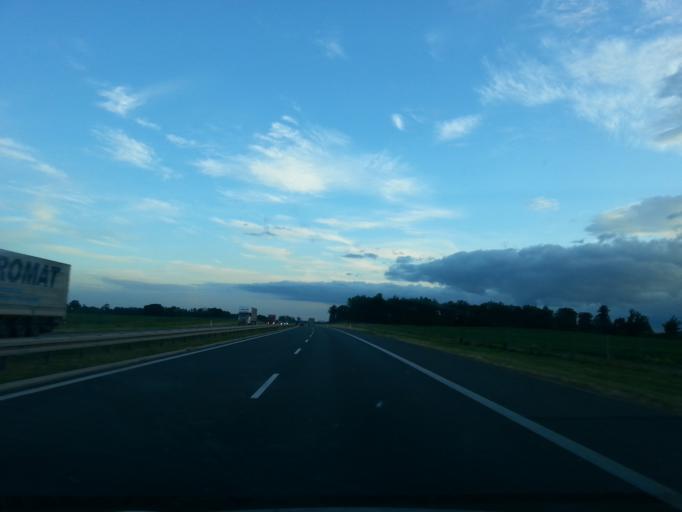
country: PL
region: Lower Silesian Voivodeship
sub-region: Powiat olesnicki
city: Twardogora
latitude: 51.2726
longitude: 17.5561
